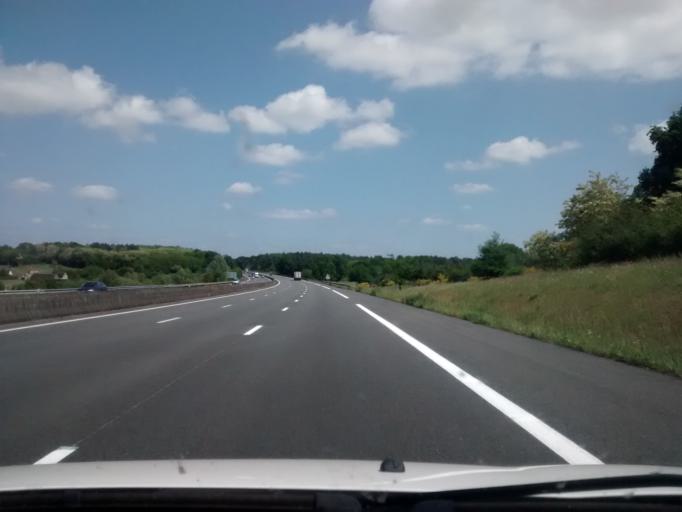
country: FR
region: Pays de la Loire
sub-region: Departement de la Sarthe
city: Connerre
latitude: 48.0748
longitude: 0.4661
